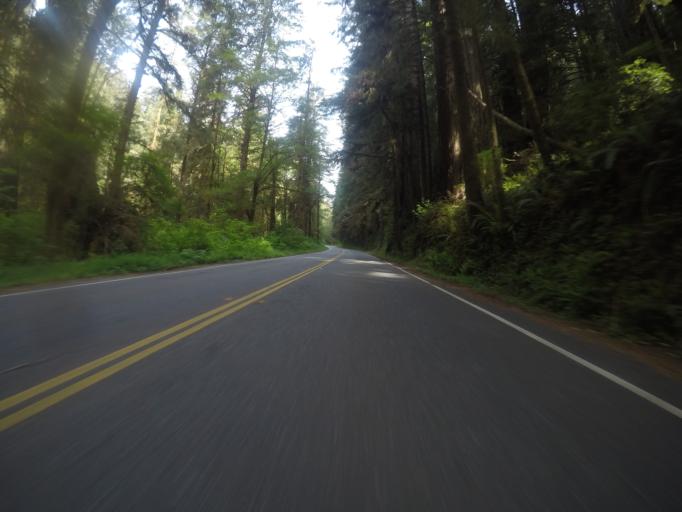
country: US
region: California
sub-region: Del Norte County
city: Bertsch-Oceanview
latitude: 41.4214
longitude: -124.0346
